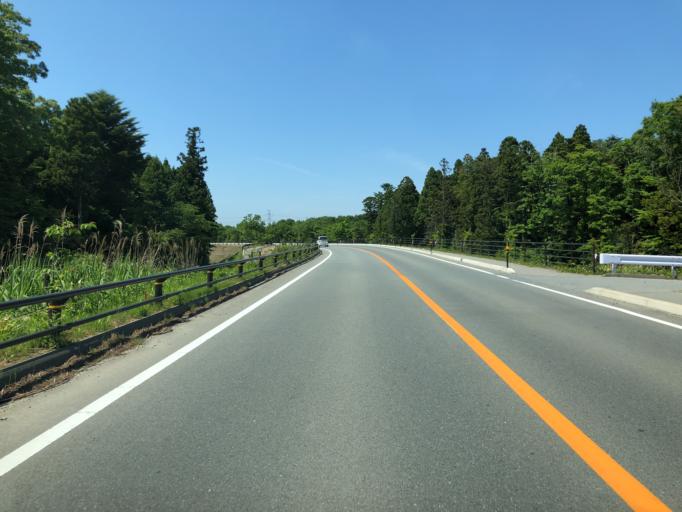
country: JP
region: Fukushima
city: Iwaki
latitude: 37.2271
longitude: 141.0071
